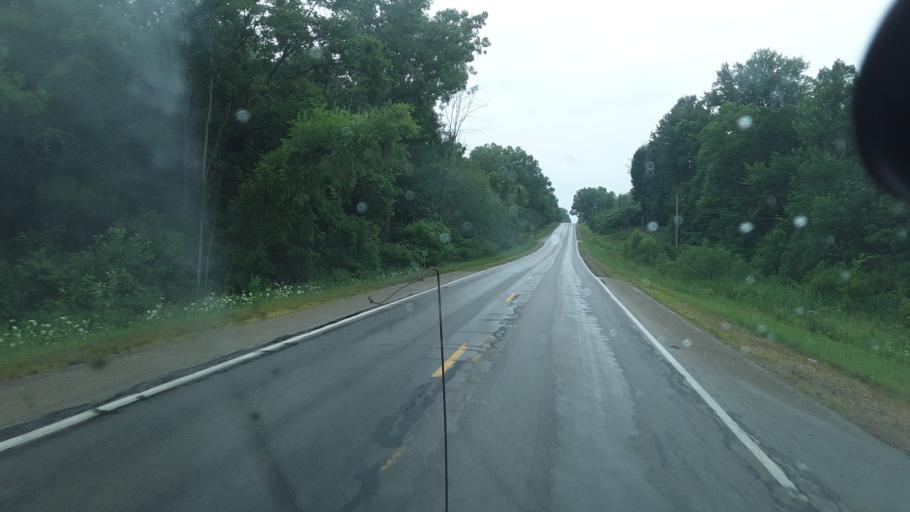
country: US
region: Indiana
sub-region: Steuben County
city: Hamilton
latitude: 41.5589
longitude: -84.8360
